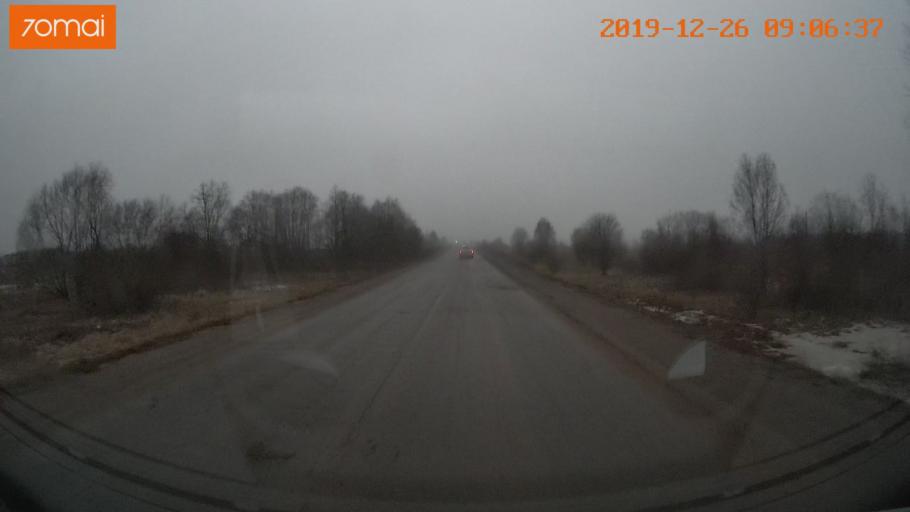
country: RU
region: Vologda
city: Gryazovets
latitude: 58.8380
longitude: 40.2528
